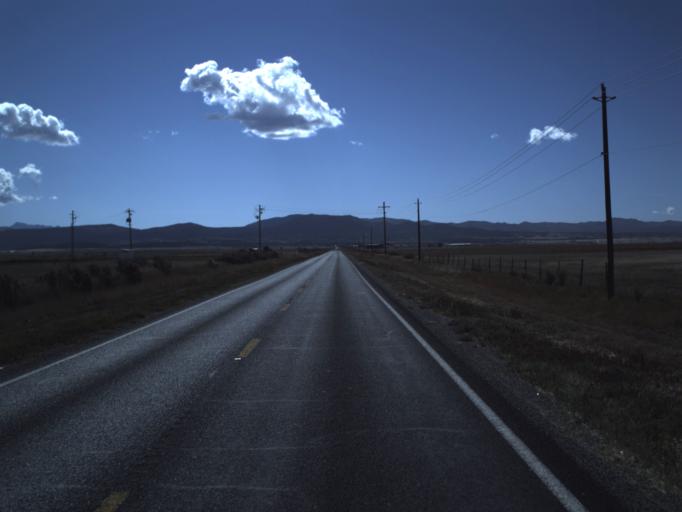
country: US
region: Utah
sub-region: Washington County
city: Enterprise
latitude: 37.6434
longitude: -113.6612
